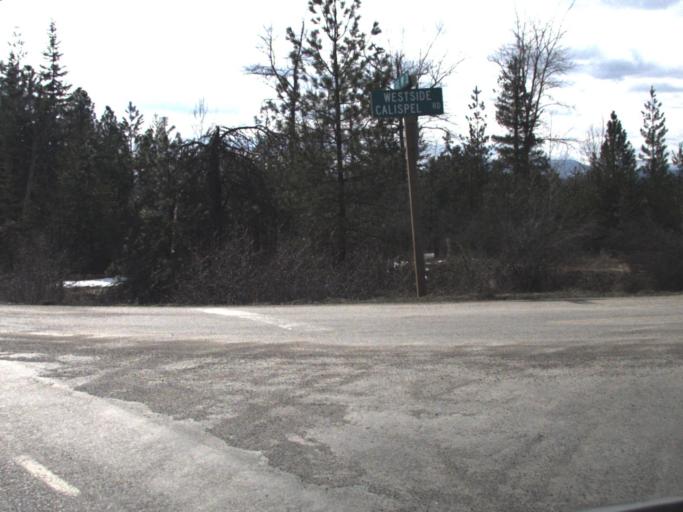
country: US
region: Washington
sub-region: Pend Oreille County
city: Newport
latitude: 48.3873
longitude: -117.3120
